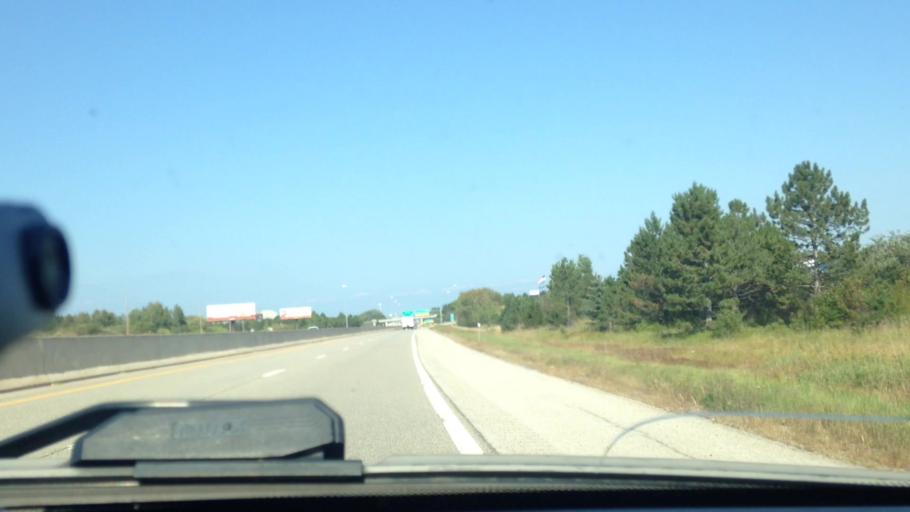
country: US
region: Michigan
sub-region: Chippewa County
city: Sault Ste. Marie
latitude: 46.4859
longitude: -84.3780
